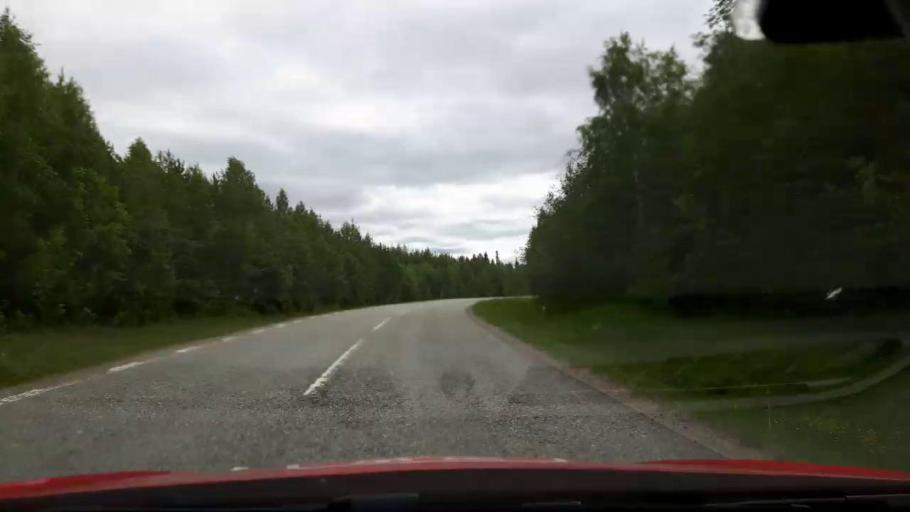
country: SE
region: Jaemtland
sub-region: Ragunda Kommun
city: Hammarstrand
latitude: 63.0396
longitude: 16.3915
